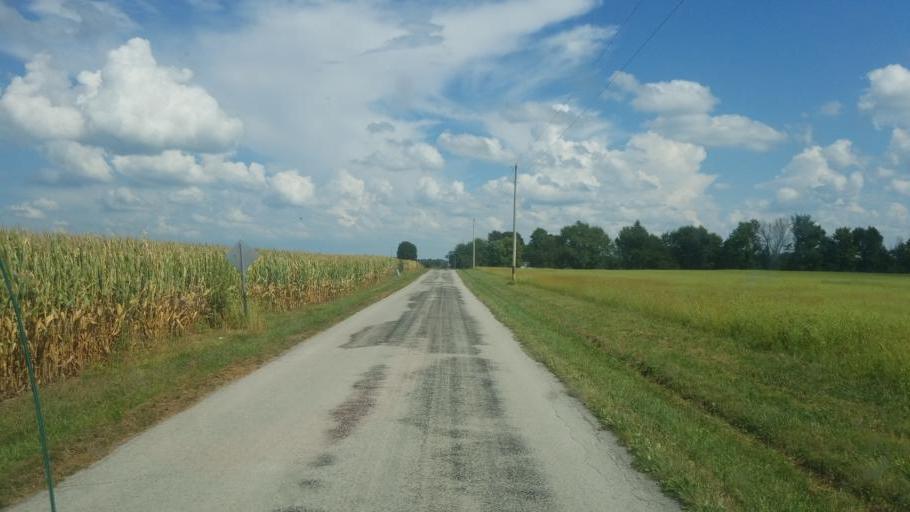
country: US
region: Ohio
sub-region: Seneca County
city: Tiffin
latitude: 40.9786
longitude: -83.1680
